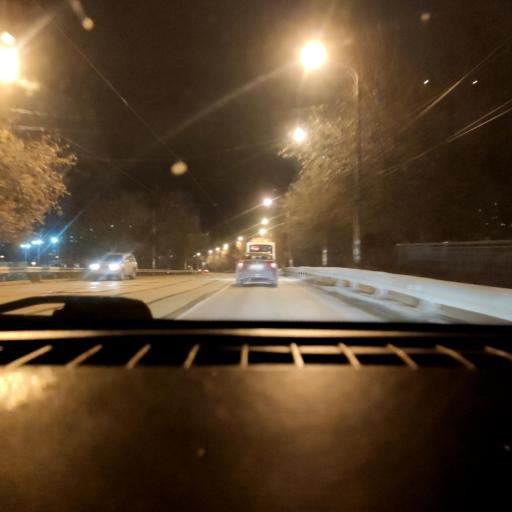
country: RU
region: Perm
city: Perm
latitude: 57.9923
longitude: 56.2183
